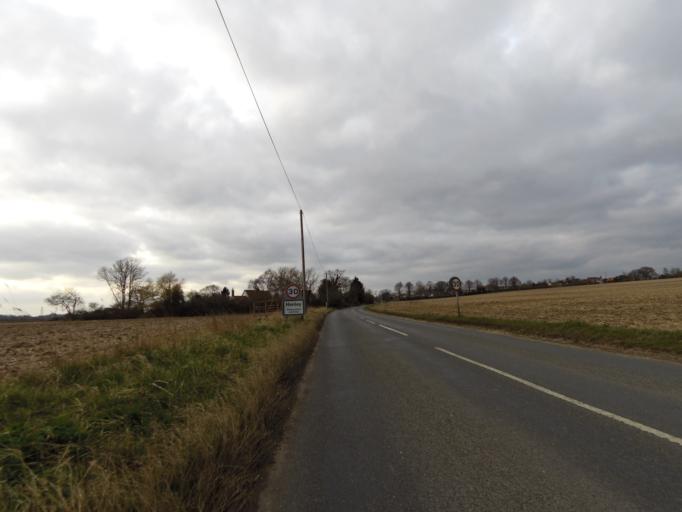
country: GB
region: England
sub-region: Suffolk
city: Ipswich
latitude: 52.1130
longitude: 1.1516
